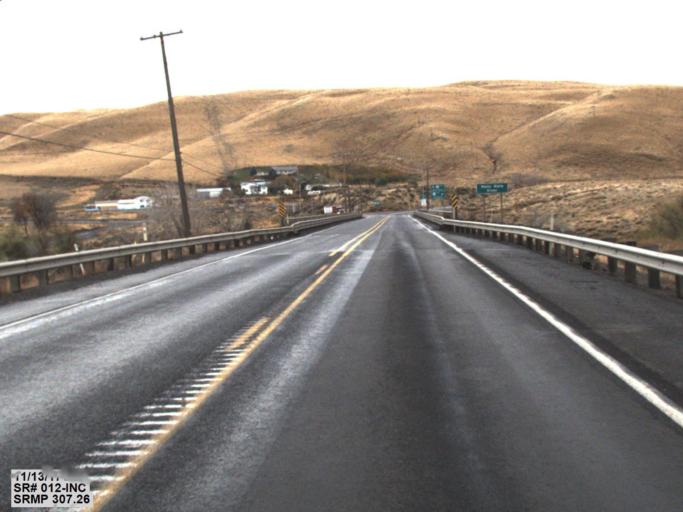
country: US
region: Washington
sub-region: Benton County
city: Finley
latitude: 46.0614
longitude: -118.9092
